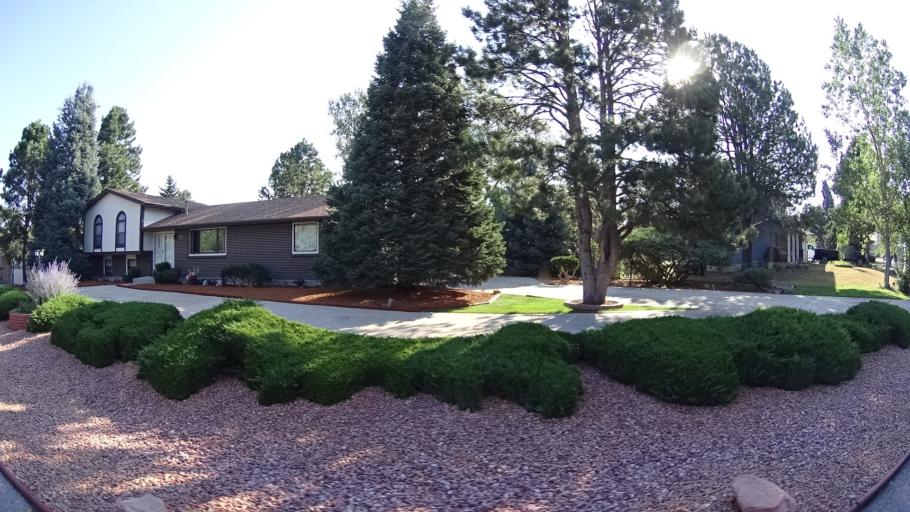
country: US
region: Colorado
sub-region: El Paso County
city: Air Force Academy
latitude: 38.9315
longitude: -104.7999
